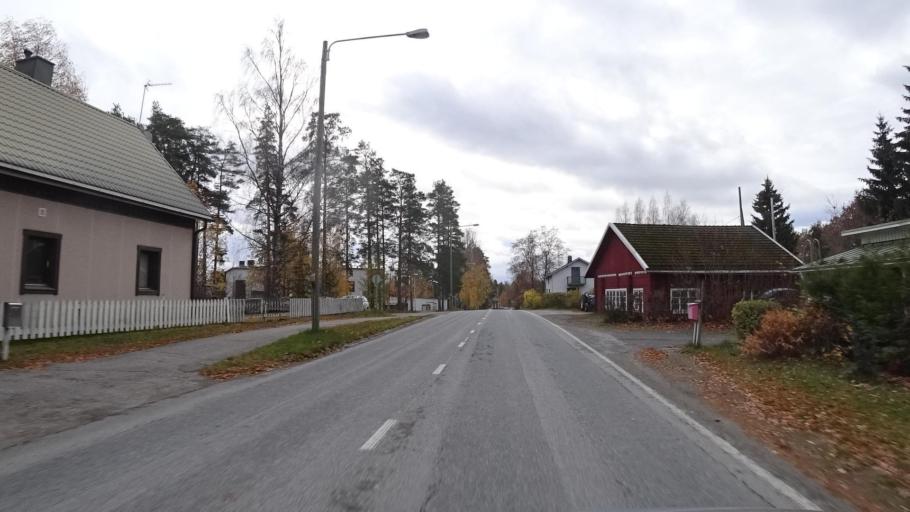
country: FI
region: Central Finland
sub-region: Joutsa
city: Joutsa
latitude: 61.7478
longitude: 26.1216
